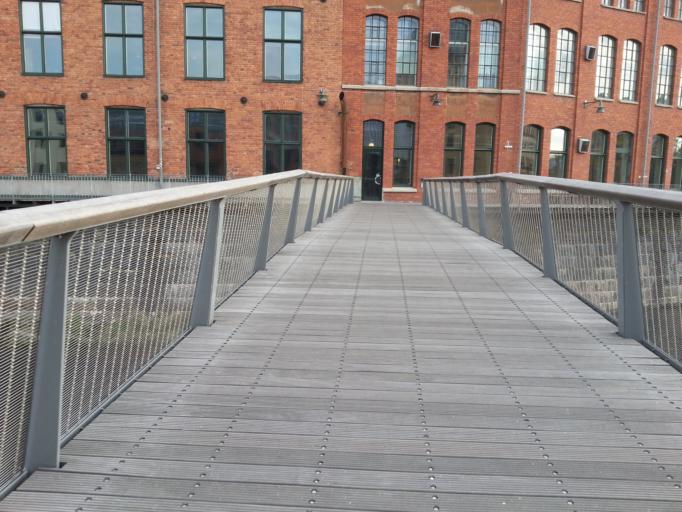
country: SE
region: OEstergoetland
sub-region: Norrkopings Kommun
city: Norrkoping
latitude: 58.5894
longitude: 16.1767
